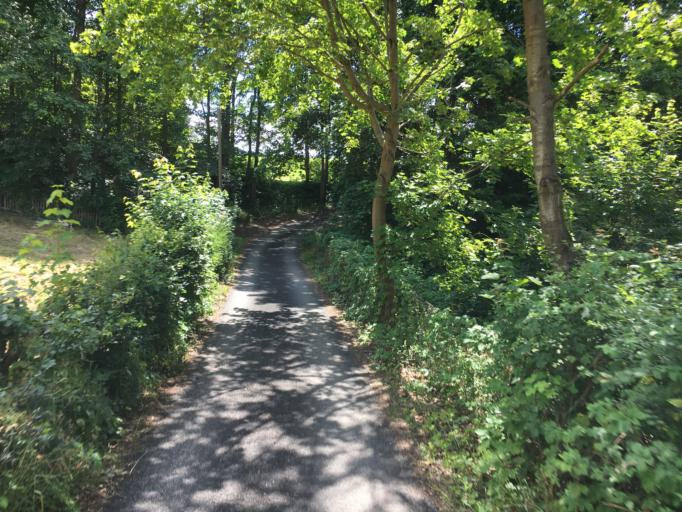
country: DE
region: Thuringia
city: Schmalkalden
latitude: 50.7251
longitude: 10.4606
